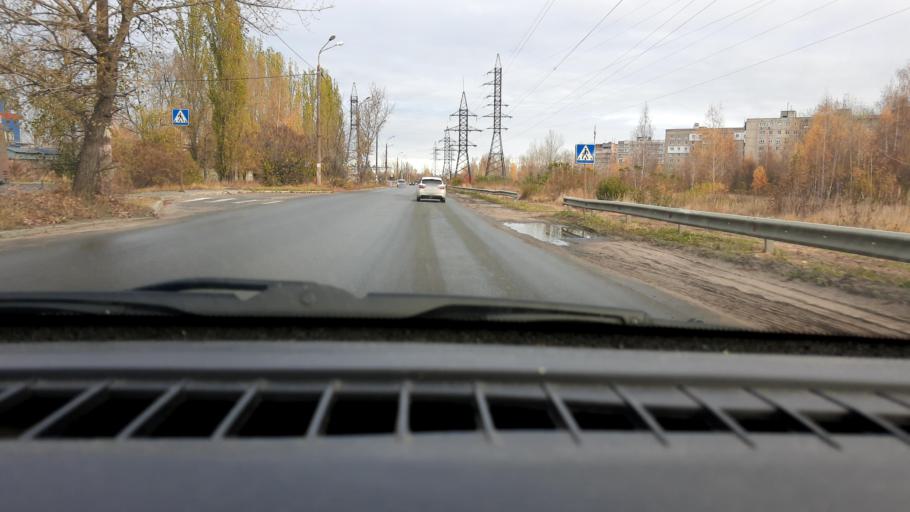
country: RU
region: Nizjnij Novgorod
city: Gorbatovka
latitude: 56.3676
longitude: 43.7964
